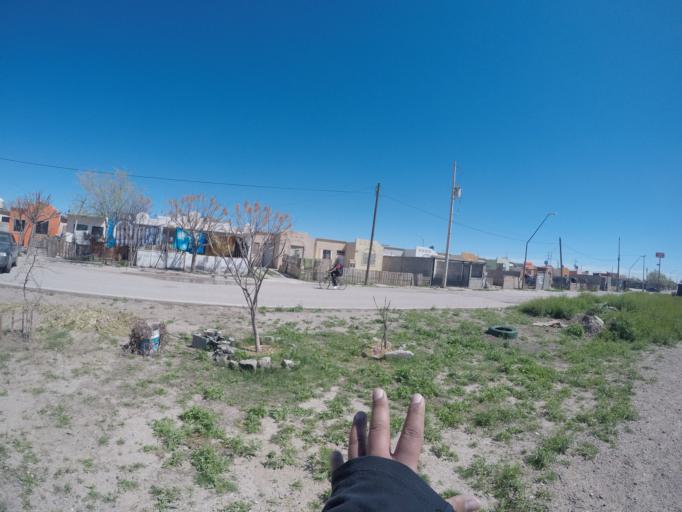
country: US
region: Texas
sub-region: El Paso County
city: Socorro Mission Number 1 Colonia
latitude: 31.6048
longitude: -106.3099
